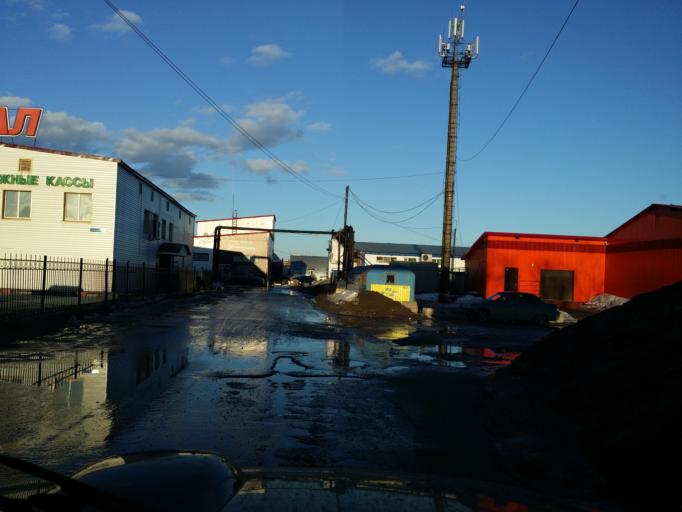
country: RU
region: Khanty-Mansiyskiy Avtonomnyy Okrug
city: Nizhnevartovsk
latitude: 60.9414
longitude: 76.5310
